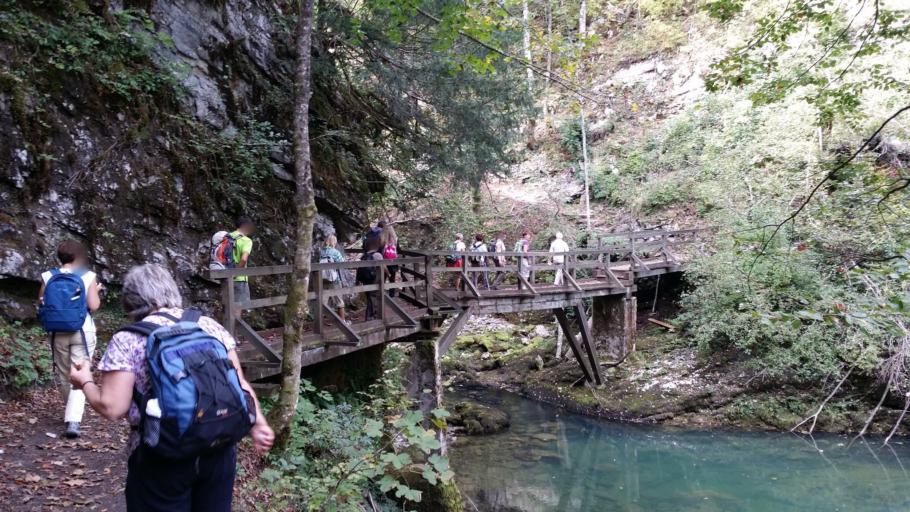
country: HR
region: Primorsko-Goranska
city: Vrbovsko
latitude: 45.3651
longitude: 15.0698
